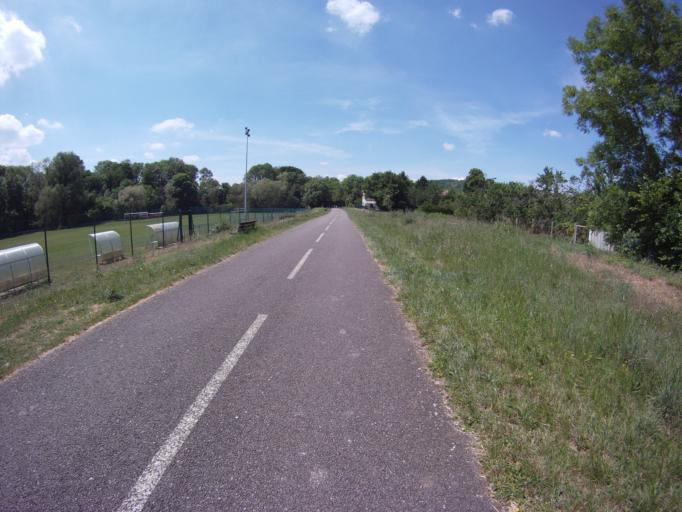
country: FR
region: Lorraine
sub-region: Departement de Meurthe-et-Moselle
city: Lay-Saint-Christophe
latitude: 48.7461
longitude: 6.2033
